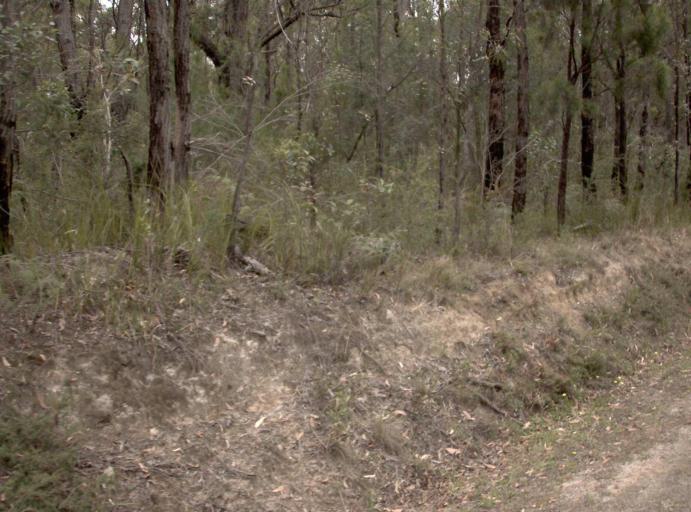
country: AU
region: Victoria
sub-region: Latrobe
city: Traralgon
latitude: -38.4757
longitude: 146.8220
